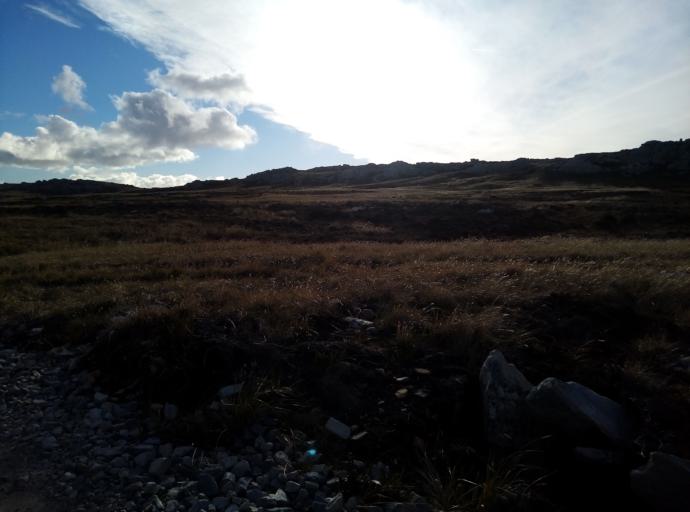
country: FK
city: Stanley
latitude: -51.6843
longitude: -57.8966
